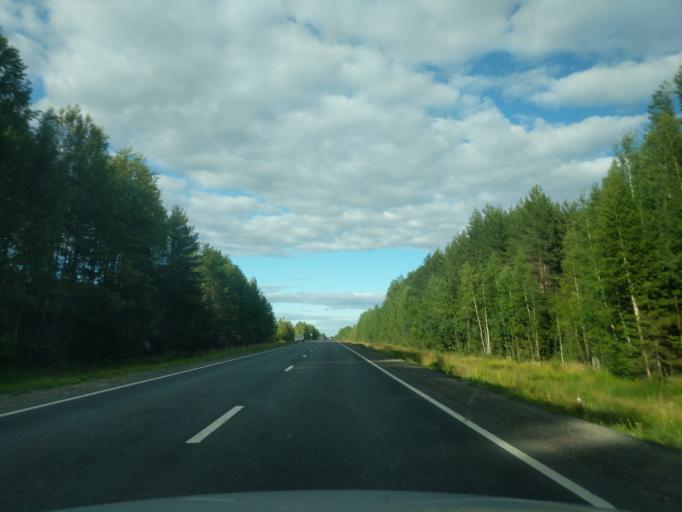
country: RU
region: Kostroma
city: Manturovo
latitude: 58.2260
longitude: 44.6258
